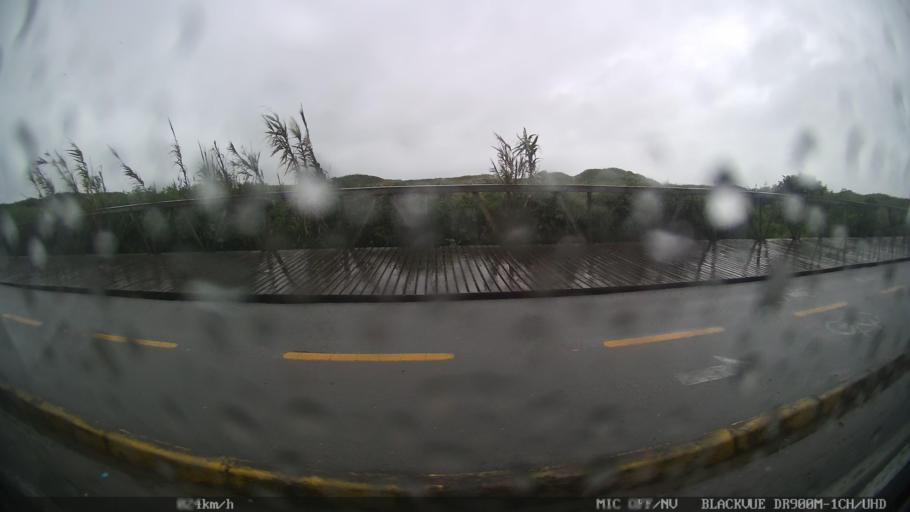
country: BR
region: Santa Catarina
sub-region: Navegantes
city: Navegantes
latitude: -26.8893
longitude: -48.6423
